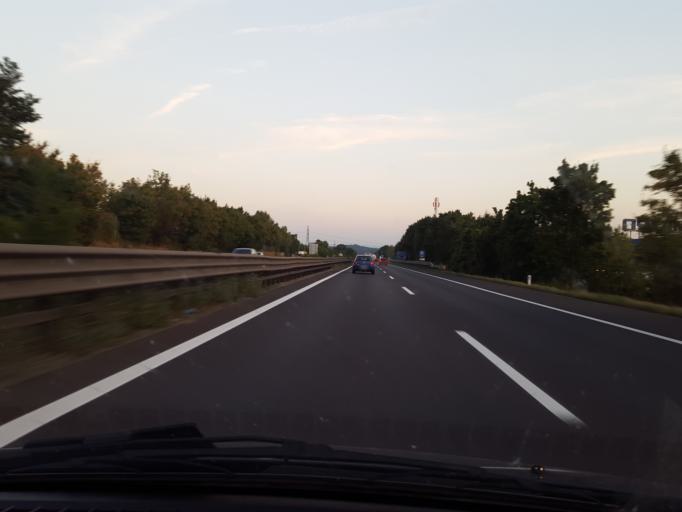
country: AT
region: Upper Austria
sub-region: Politischer Bezirk Linz-Land
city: Ansfelden
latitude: 48.2492
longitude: 14.2972
